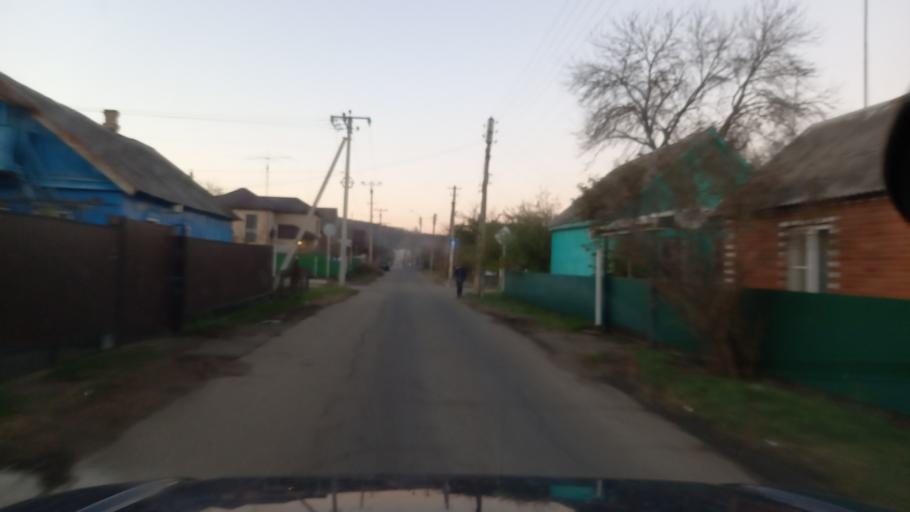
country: RU
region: Krasnodarskiy
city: Goryachiy Klyuch
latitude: 44.6297
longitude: 39.1040
